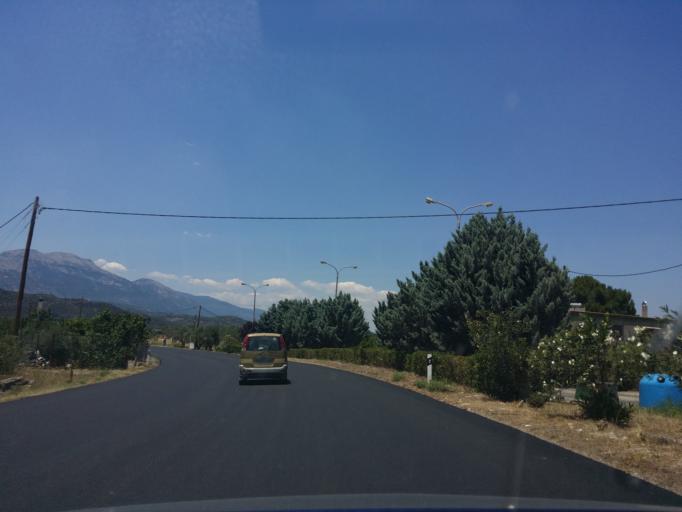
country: GR
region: Peloponnese
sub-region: Nomos Lakonias
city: Sparti
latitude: 37.0876
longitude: 22.4429
